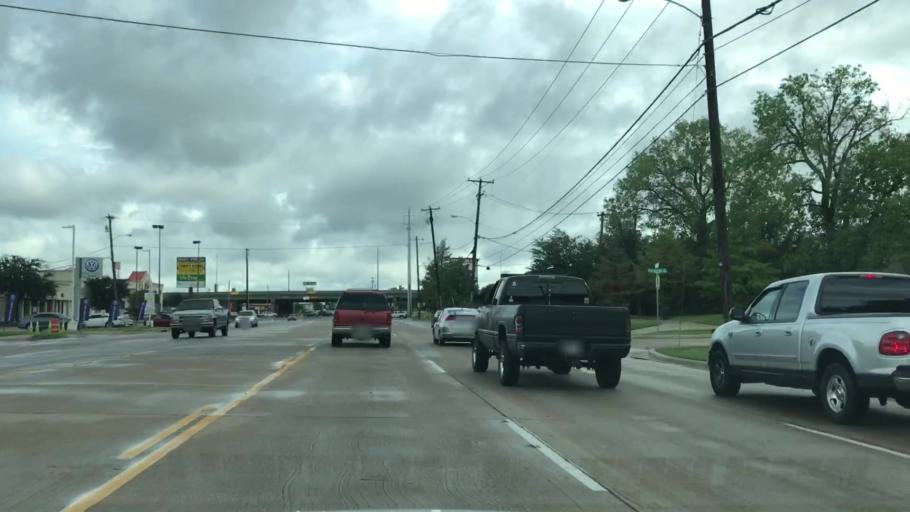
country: US
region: Texas
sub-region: Dallas County
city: Irving
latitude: 32.8399
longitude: -96.9766
